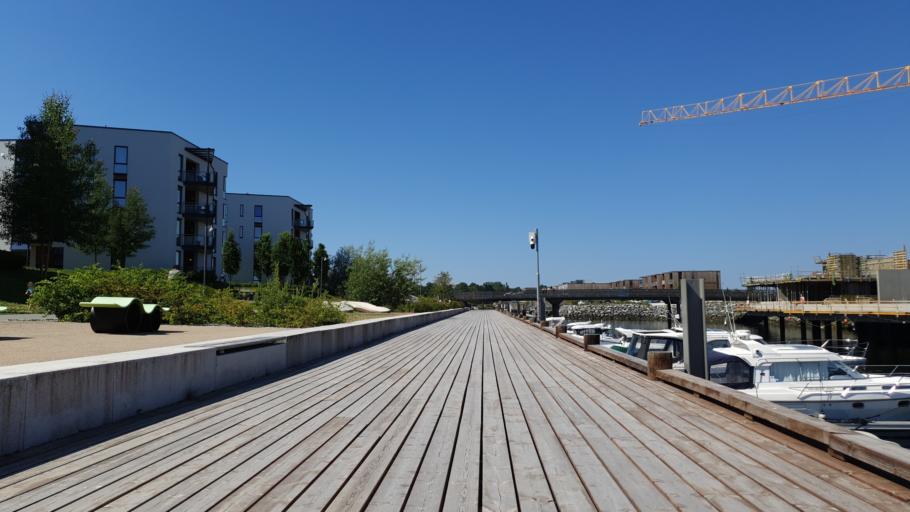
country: NO
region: Sor-Trondelag
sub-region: Trondheim
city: Trondheim
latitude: 63.4359
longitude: 10.5095
